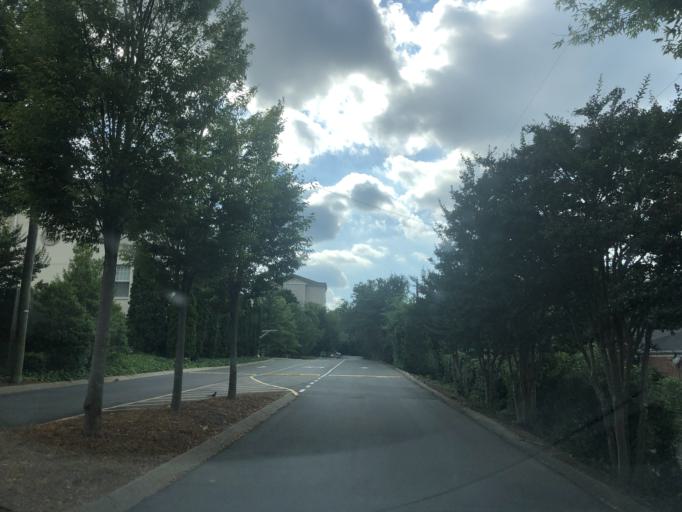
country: US
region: Tennessee
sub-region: Davidson County
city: Belle Meade
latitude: 36.0981
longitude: -86.8254
